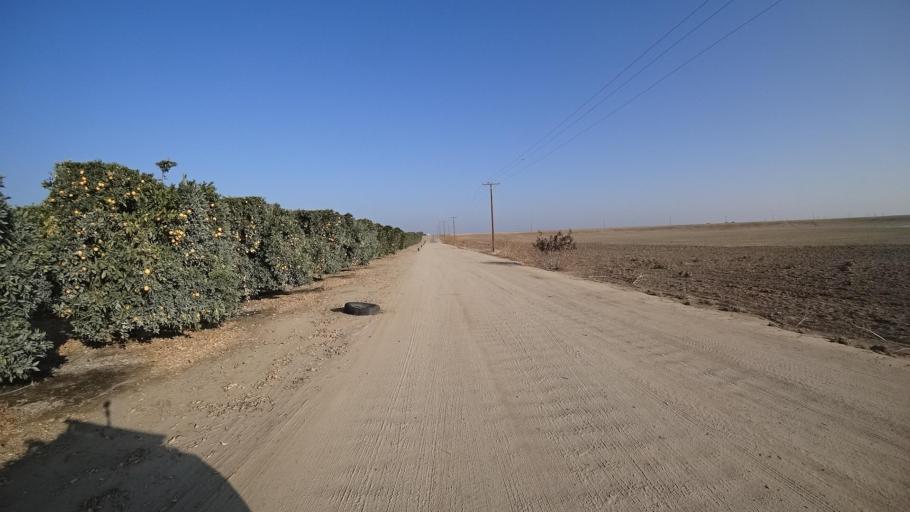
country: US
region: California
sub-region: Tulare County
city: Richgrove
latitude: 35.7727
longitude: -119.0807
